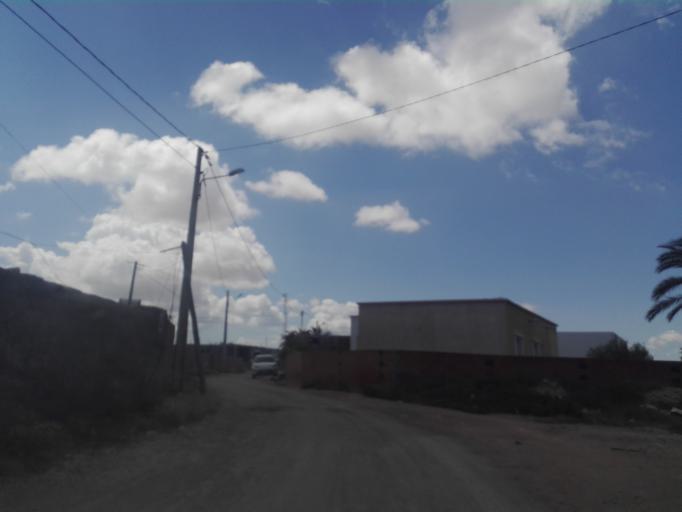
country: TN
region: Safaqis
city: Jabinyanah
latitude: 34.8220
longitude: 11.2532
